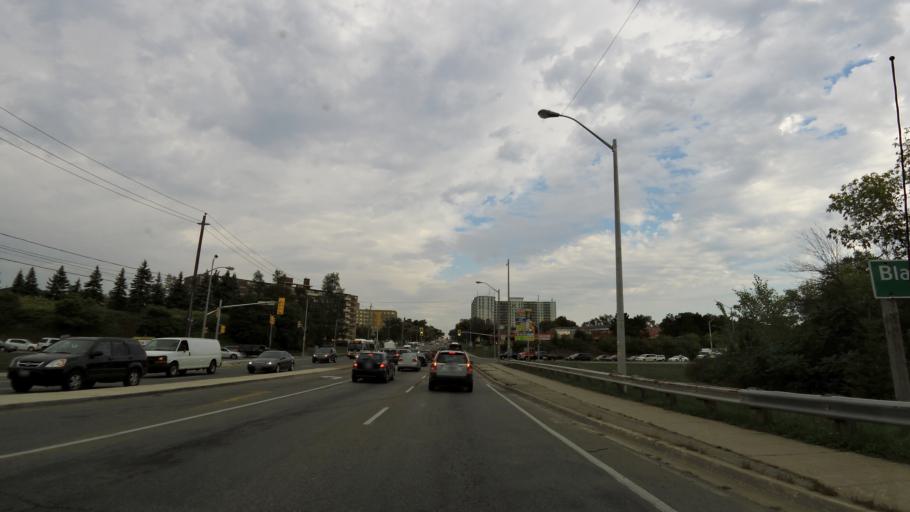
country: CA
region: Ontario
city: Toronto
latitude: 43.7046
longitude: -79.4951
